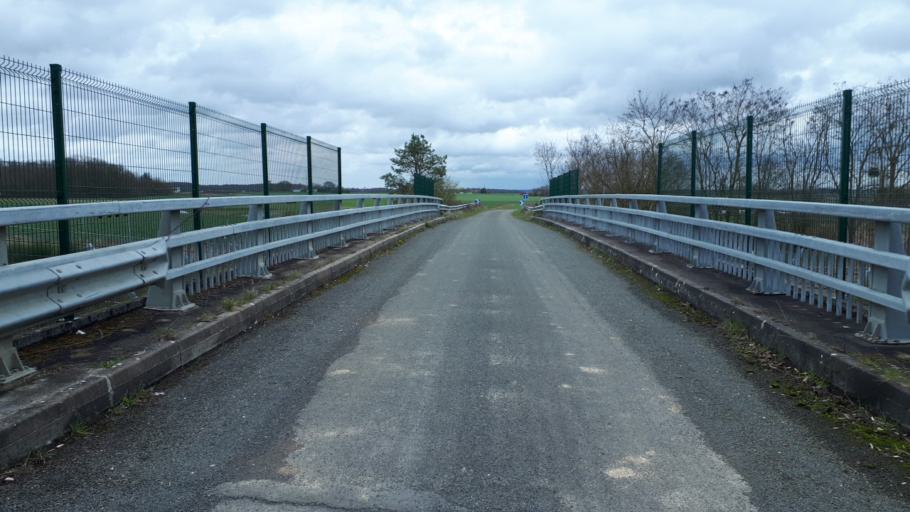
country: FR
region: Centre
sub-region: Departement du Loir-et-Cher
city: Villiers-sur-Loir
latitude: 47.8091
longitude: 1.0146
